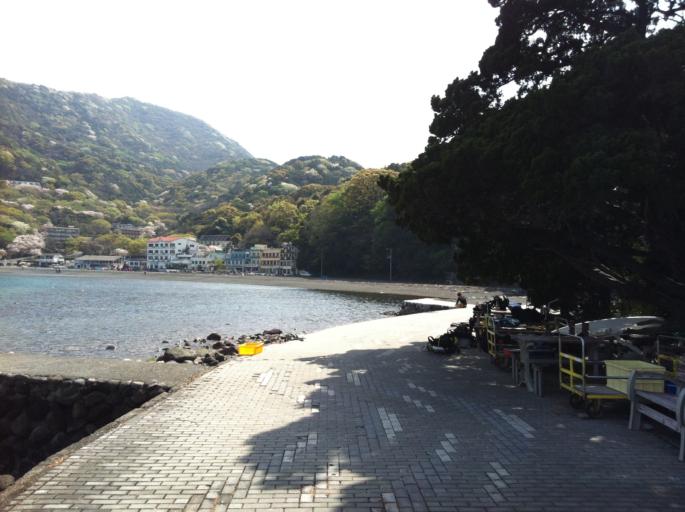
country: JP
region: Shizuoka
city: Heda
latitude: 35.0274
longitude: 138.7865
